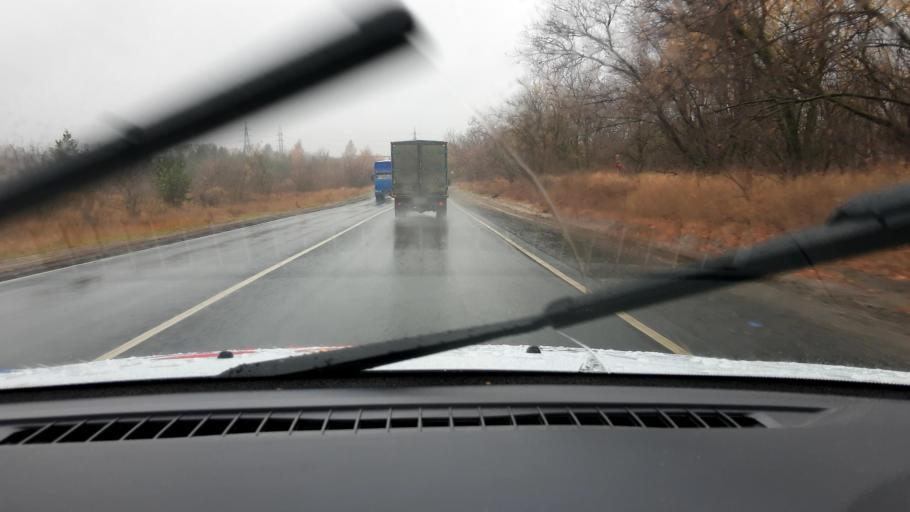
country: RU
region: Nizjnij Novgorod
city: Babino
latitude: 56.2575
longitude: 43.6232
